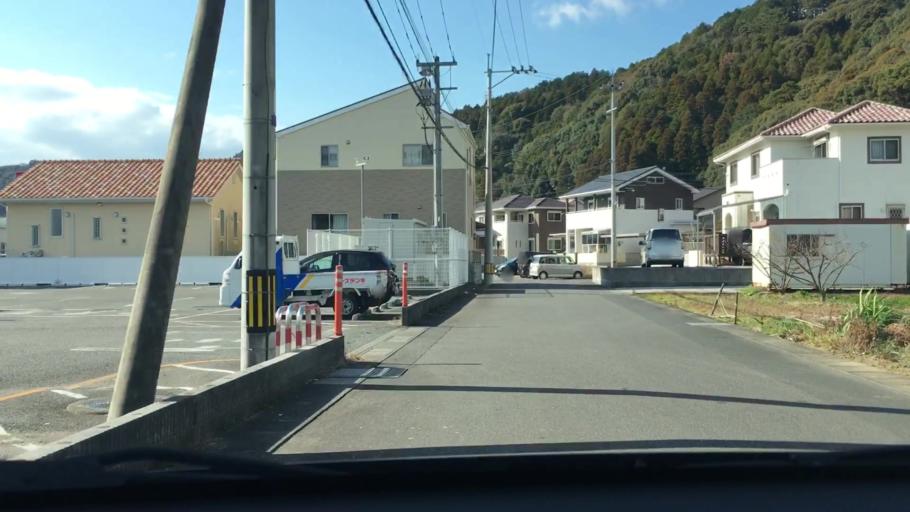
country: JP
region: Oita
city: Saiki
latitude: 32.9629
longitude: 131.8664
